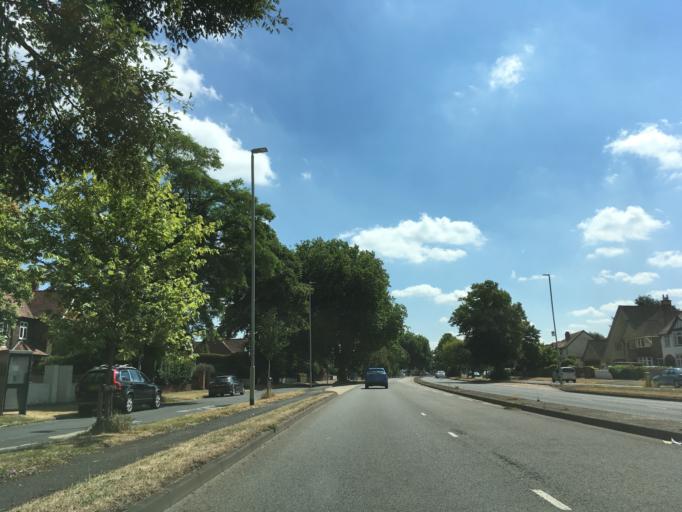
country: GB
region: England
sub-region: Gloucestershire
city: Gloucester
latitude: 51.8758
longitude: -2.2378
